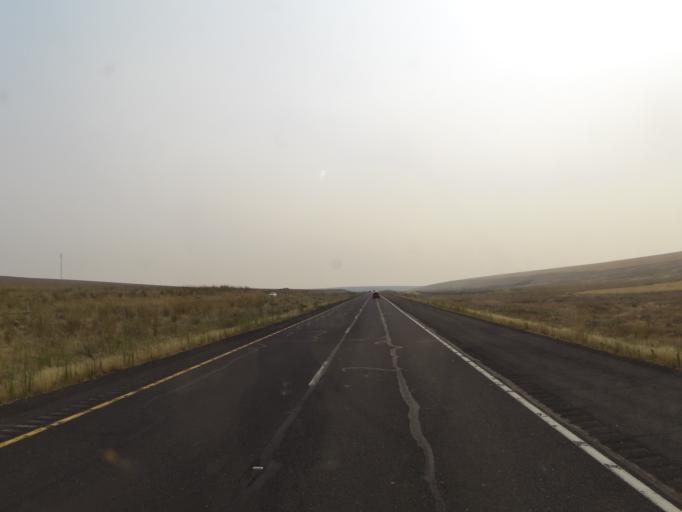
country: US
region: Washington
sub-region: Franklin County
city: Connell
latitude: 46.8345
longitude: -118.6545
